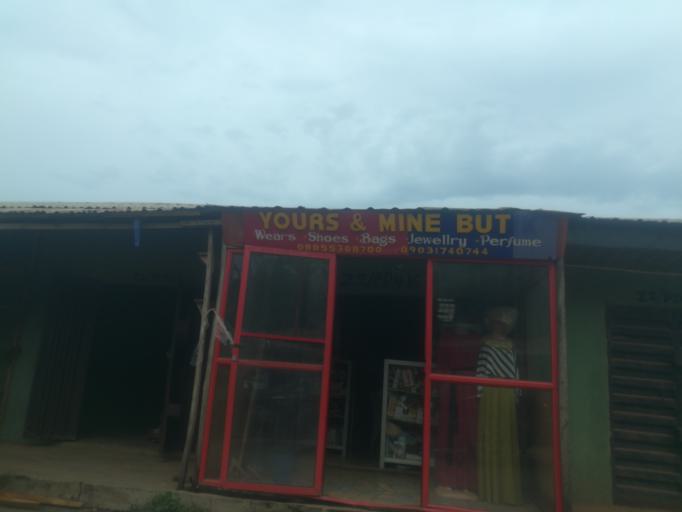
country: NG
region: Oyo
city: Ibadan
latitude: 7.3915
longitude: 3.9527
